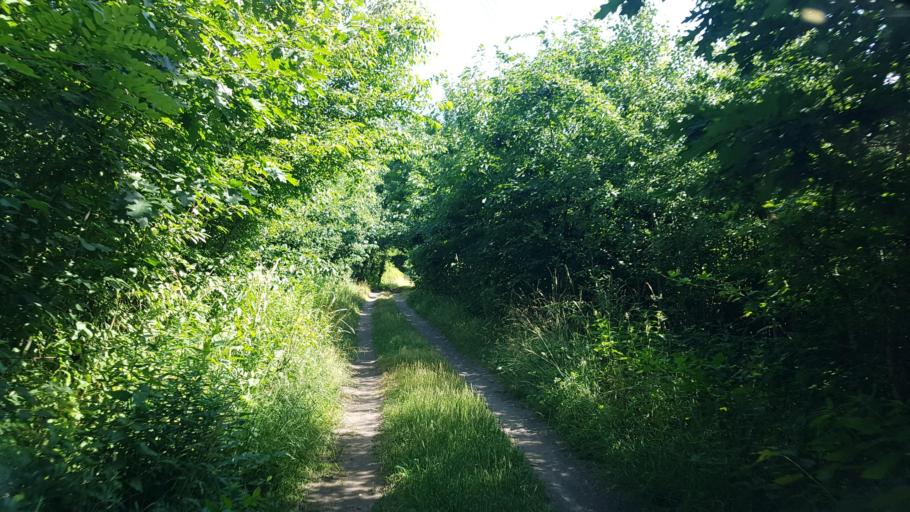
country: DE
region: Brandenburg
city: Altdobern
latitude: 51.6541
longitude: 14.0163
